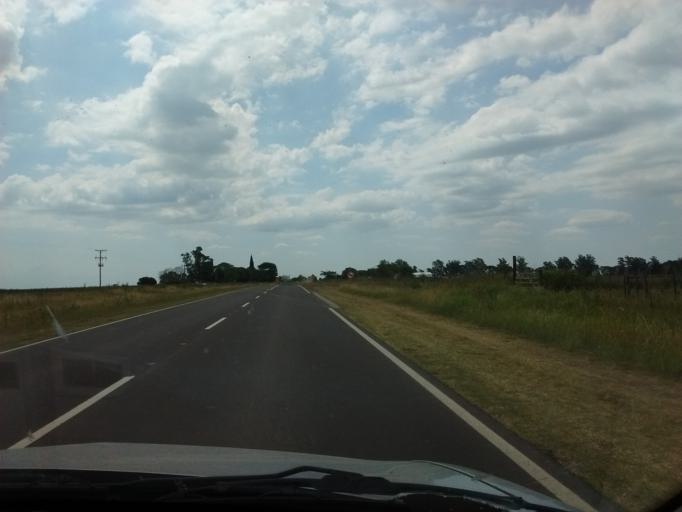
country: AR
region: Entre Rios
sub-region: Departamento de Victoria
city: Victoria
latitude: -32.7700
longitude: -59.9234
